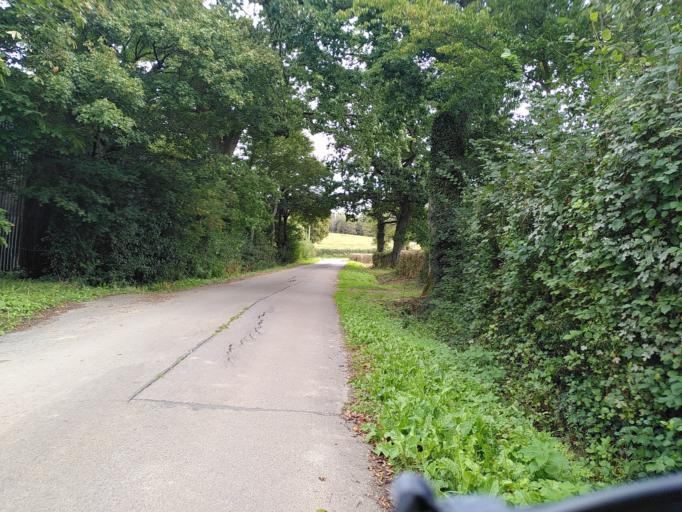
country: FR
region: Nord-Pas-de-Calais
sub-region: Departement du Pas-de-Calais
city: Longfosse
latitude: 50.6921
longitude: 1.7870
